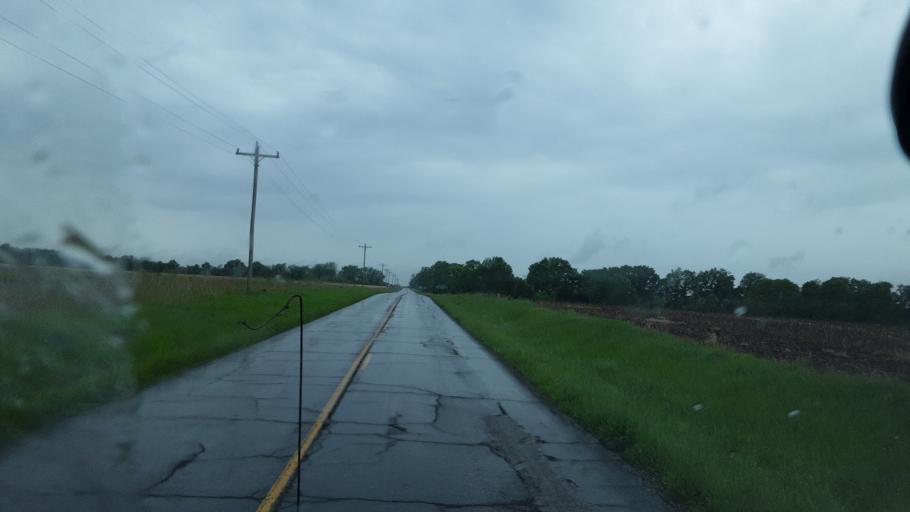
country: US
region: Missouri
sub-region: Randolph County
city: Moberly
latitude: 39.3930
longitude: -92.2441
